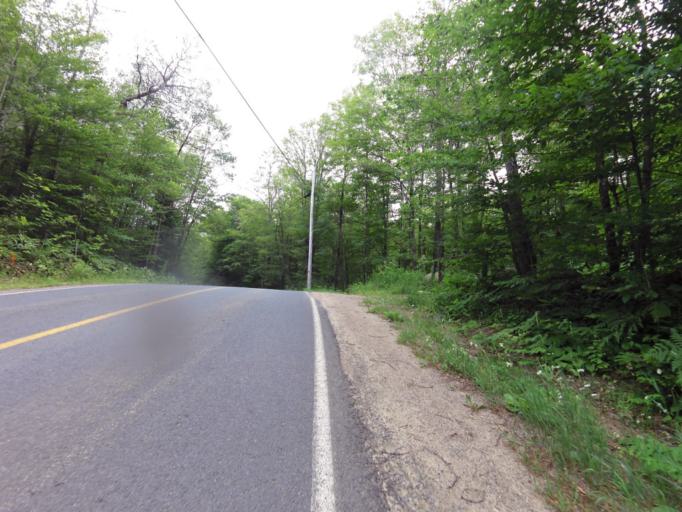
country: CA
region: Quebec
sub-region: Laurentides
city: Brownsburg-Chatham
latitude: 45.8892
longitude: -74.5909
